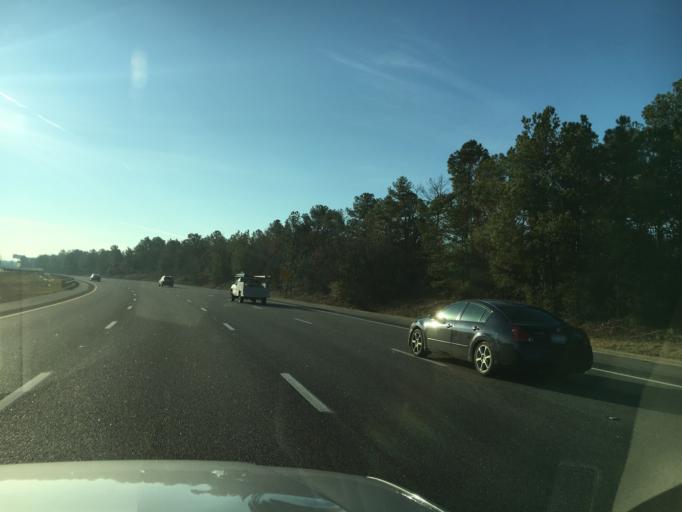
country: US
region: South Carolina
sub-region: Lexington County
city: Pineridge
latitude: 33.9218
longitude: -81.0679
